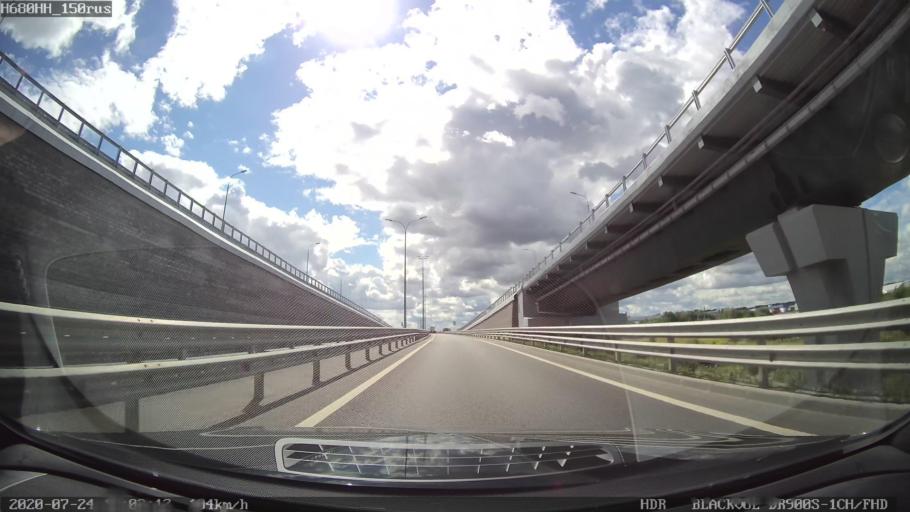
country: RU
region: St.-Petersburg
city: Shushary
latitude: 59.8057
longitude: 30.3338
